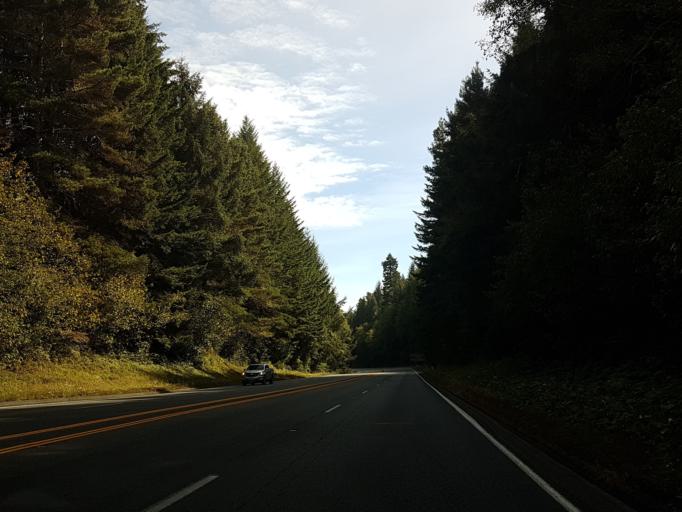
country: US
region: California
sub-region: Del Norte County
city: Bertsch-Oceanview
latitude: 41.4792
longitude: -124.0482
